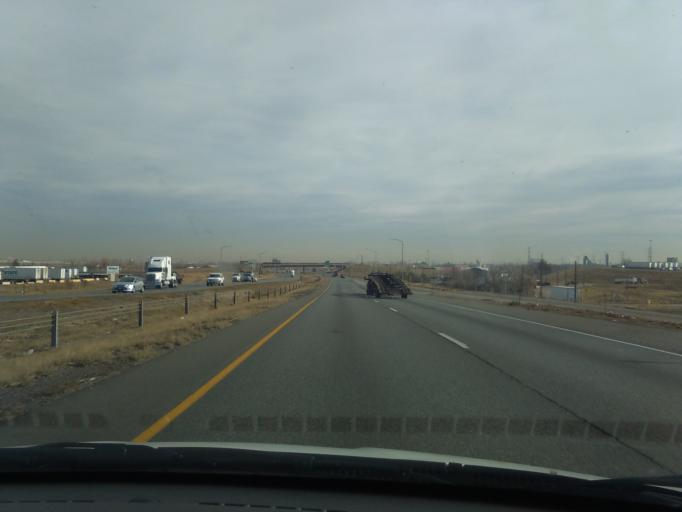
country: US
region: Colorado
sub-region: Adams County
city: Twin Lakes
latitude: 39.8092
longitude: -105.0039
